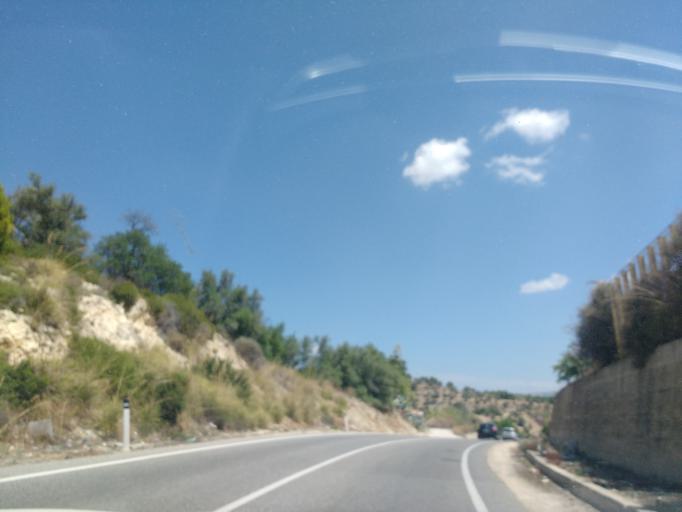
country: IT
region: Sicily
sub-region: Provincia di Siracusa
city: Noto
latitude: 36.8658
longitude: 15.0241
